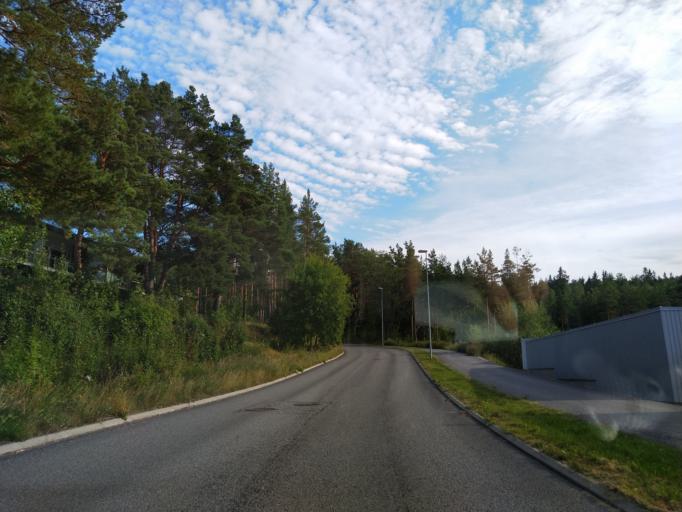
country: FI
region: Varsinais-Suomi
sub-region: Turku
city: Turku
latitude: 60.4252
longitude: 22.2078
